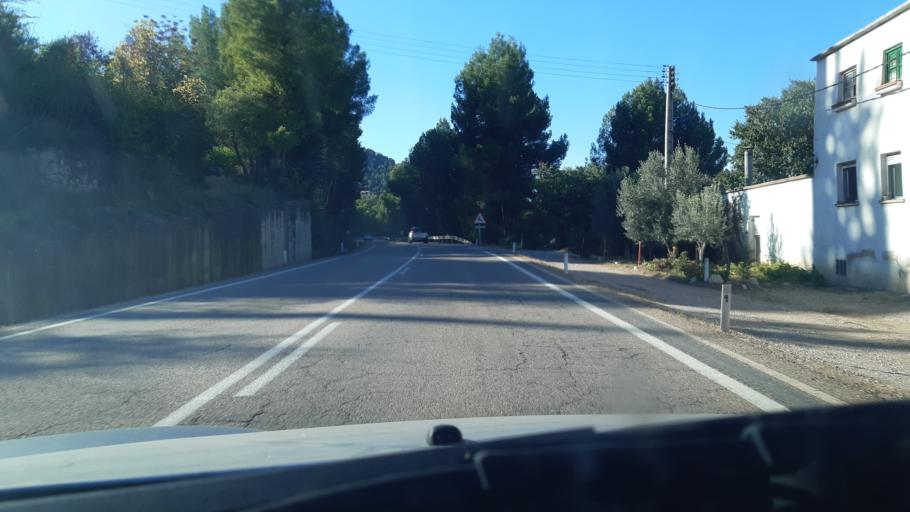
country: ES
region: Aragon
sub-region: Provincia de Teruel
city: Valderrobres
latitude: 40.8729
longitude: 0.1428
